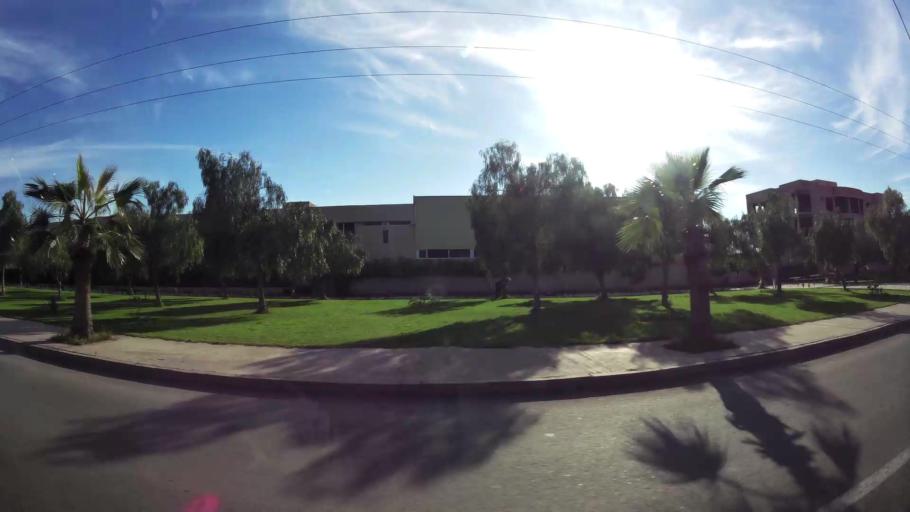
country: MA
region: Marrakech-Tensift-Al Haouz
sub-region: Marrakech
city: Marrakesh
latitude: 31.6832
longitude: -8.0507
